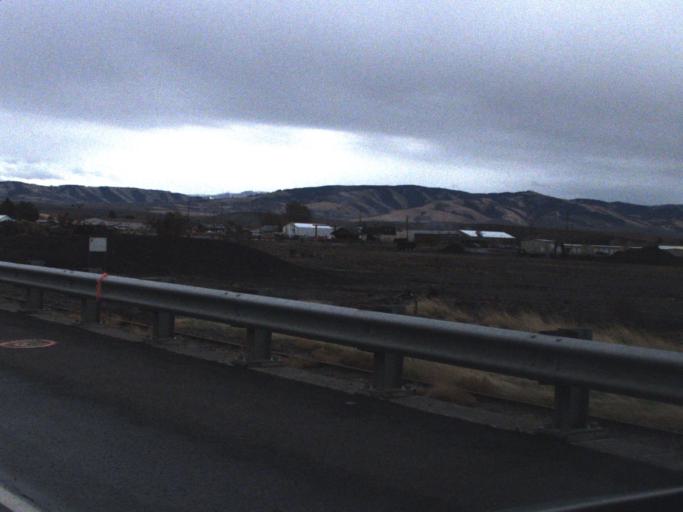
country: US
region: Washington
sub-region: Walla Walla County
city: Walla Walla East
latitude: 46.0824
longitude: -118.2938
